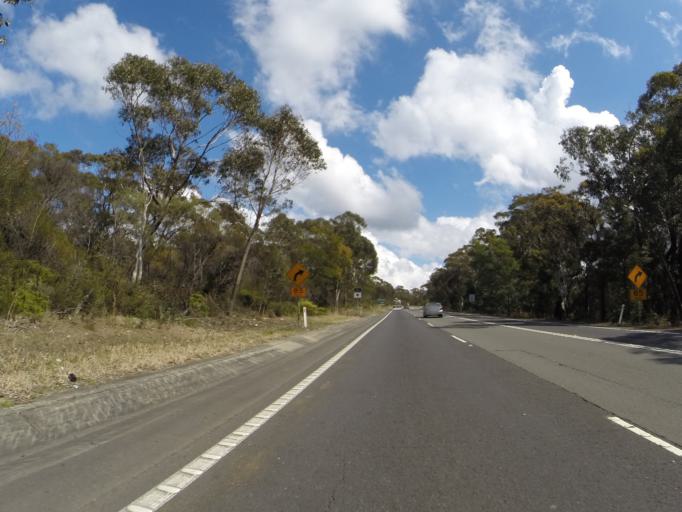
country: AU
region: New South Wales
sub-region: Wollongong
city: Mount Ousley
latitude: -34.3759
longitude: 150.8348
